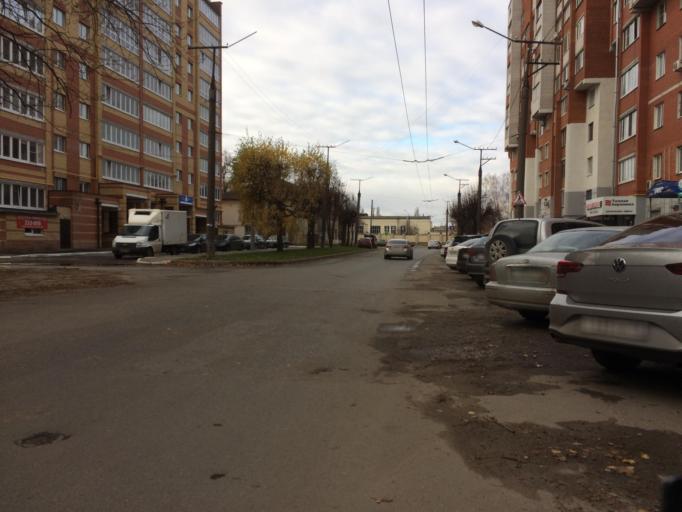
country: RU
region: Mariy-El
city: Yoshkar-Ola
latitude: 56.6397
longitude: 47.8629
